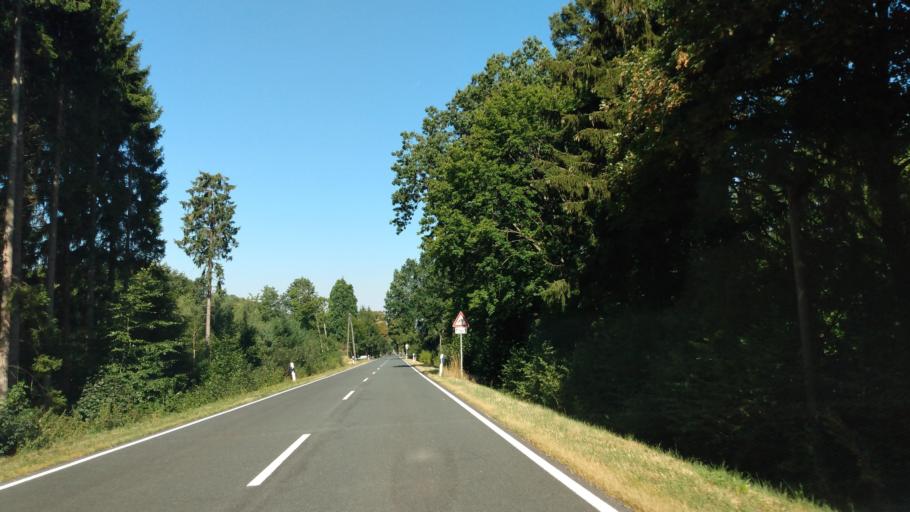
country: DE
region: Rheinland-Pfalz
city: Lotzbeuren
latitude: 49.9158
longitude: 7.2019
